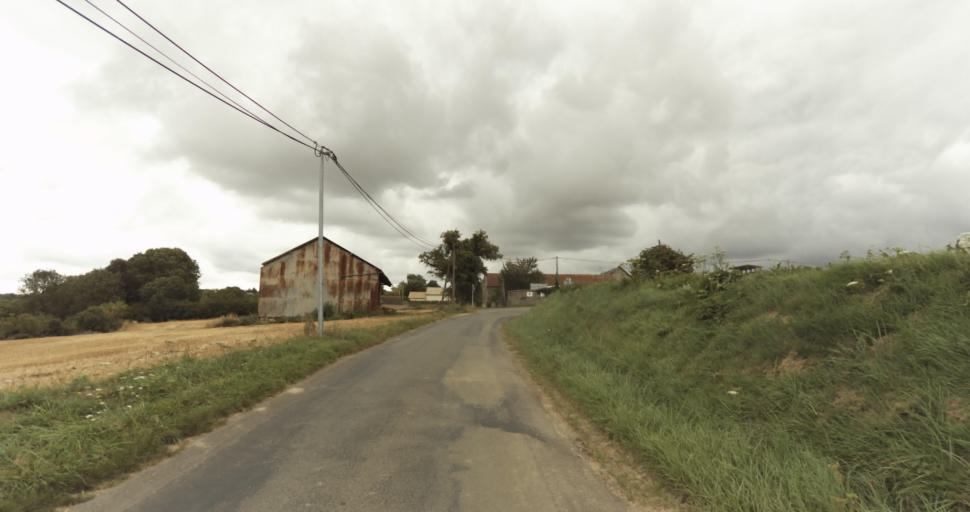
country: FR
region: Haute-Normandie
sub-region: Departement de l'Eure
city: Menilles
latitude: 49.0194
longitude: 1.3026
